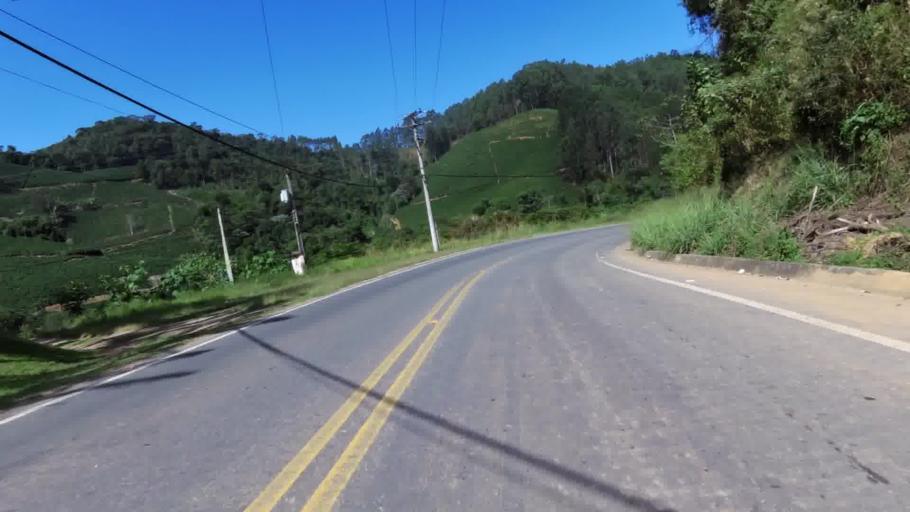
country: BR
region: Espirito Santo
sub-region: Marechal Floriano
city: Marechal Floriano
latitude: -20.4495
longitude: -40.7859
